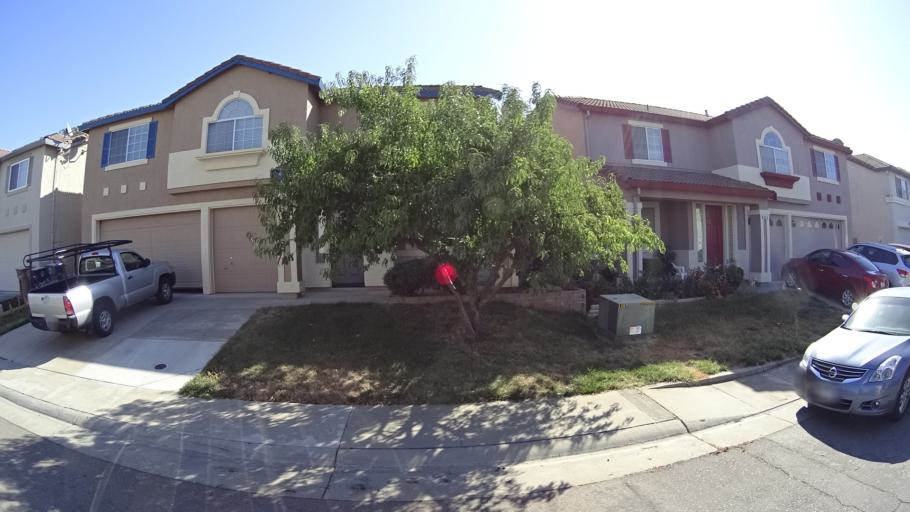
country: US
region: California
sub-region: Sacramento County
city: Laguna
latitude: 38.4397
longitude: -121.4366
